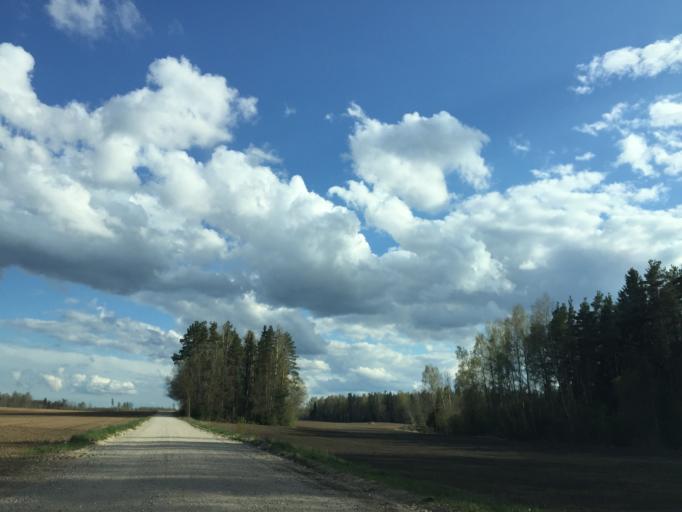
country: LV
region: Beverina
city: Murmuiza
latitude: 57.3941
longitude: 25.4787
